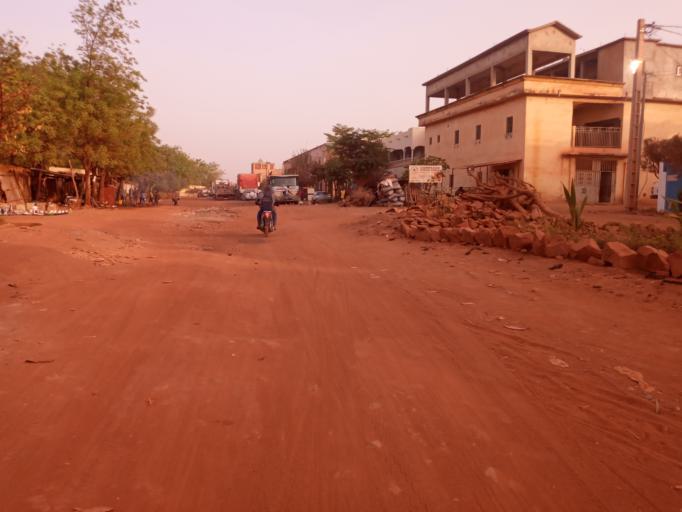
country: ML
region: Bamako
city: Bamako
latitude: 12.5940
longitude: -7.9603
